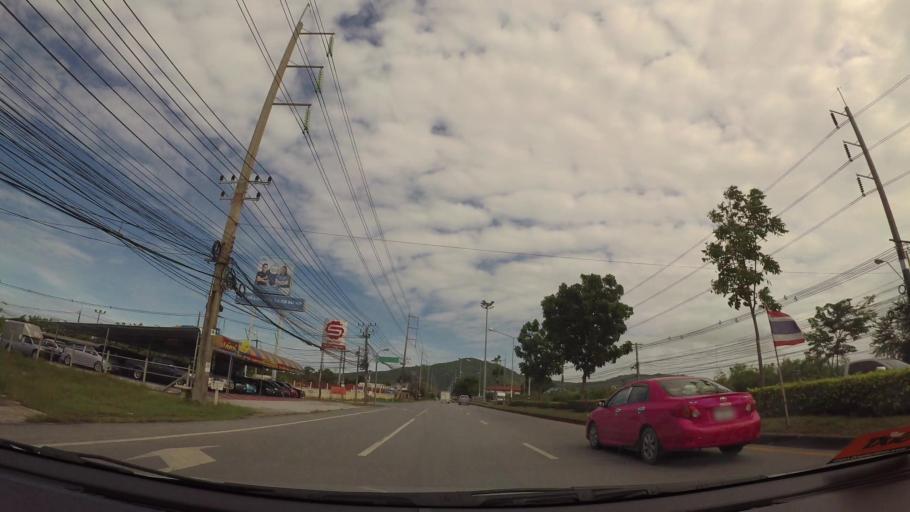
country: TH
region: Rayong
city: Ban Chang
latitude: 12.7448
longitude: 101.1144
